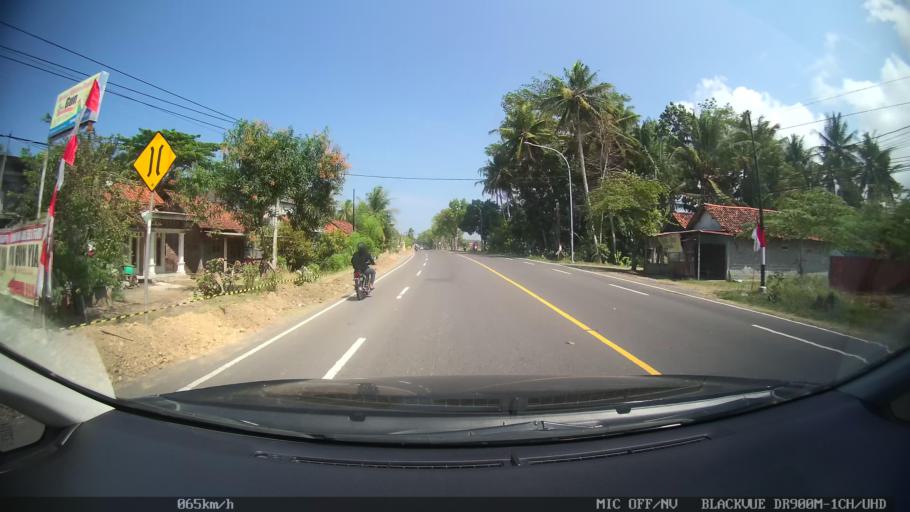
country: ID
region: Daerah Istimewa Yogyakarta
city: Srandakan
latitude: -7.8875
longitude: 110.0884
